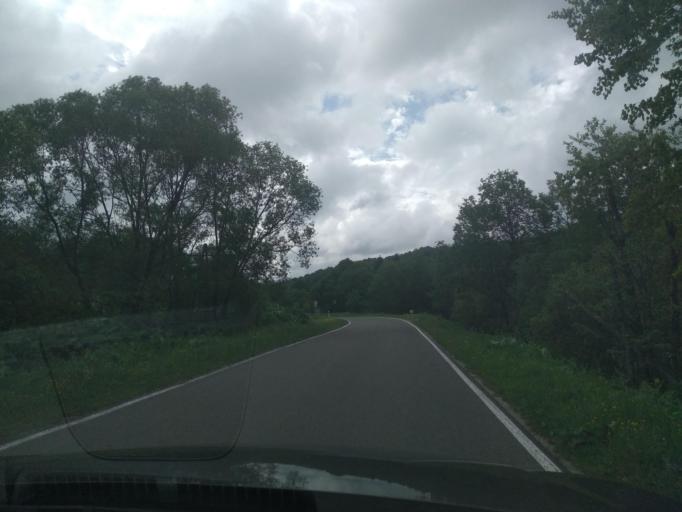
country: PL
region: Subcarpathian Voivodeship
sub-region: Powiat bieszczadzki
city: Lutowiska
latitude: 49.0822
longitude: 22.6533
